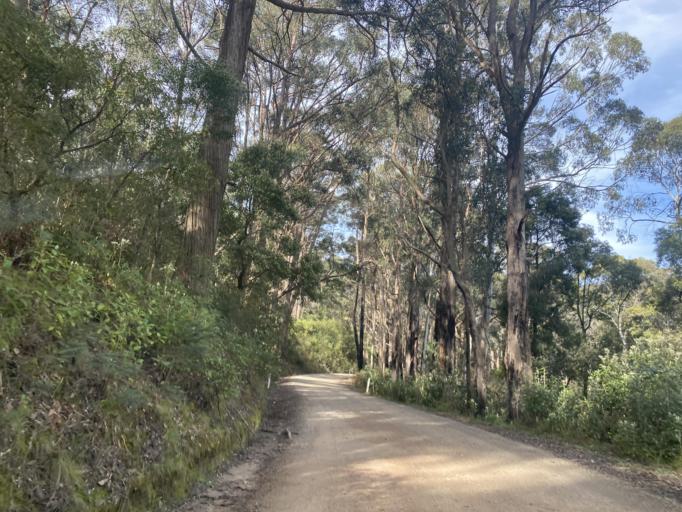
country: AU
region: Victoria
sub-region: Mansfield
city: Mansfield
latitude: -36.8435
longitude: 146.1744
